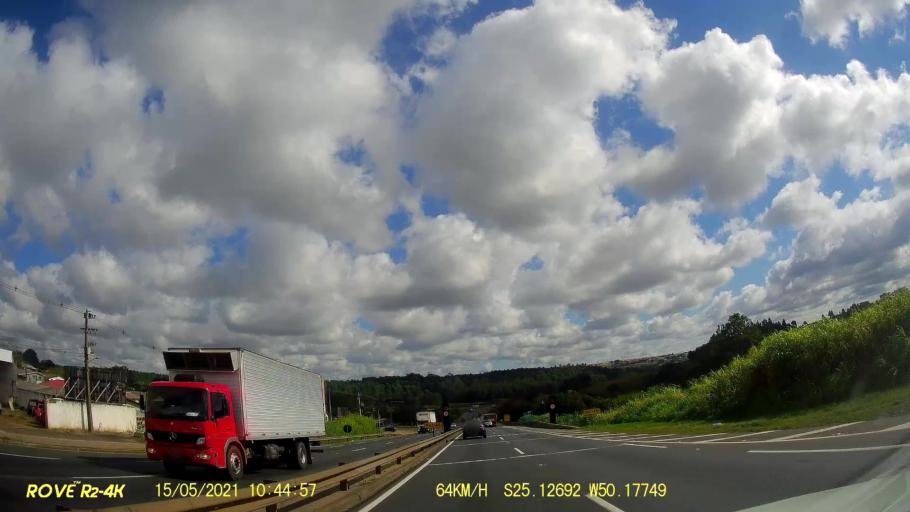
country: BR
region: Parana
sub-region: Ponta Grossa
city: Ponta Grossa
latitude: -25.1269
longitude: -50.1775
